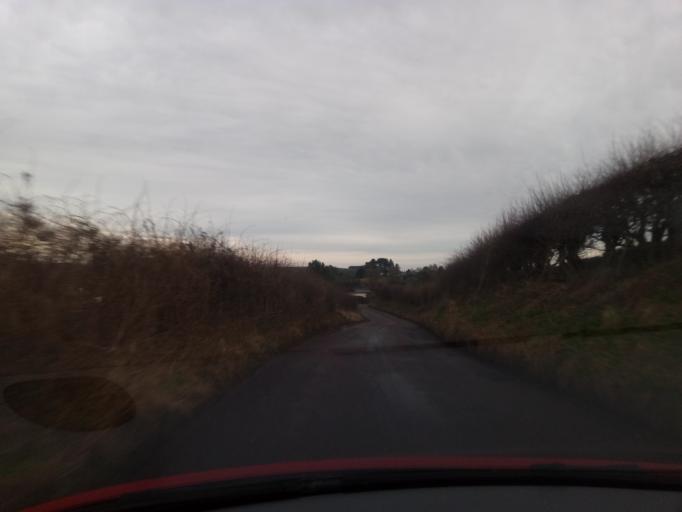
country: GB
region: England
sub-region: Northumberland
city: Wooler
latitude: 55.5516
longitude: -2.0305
